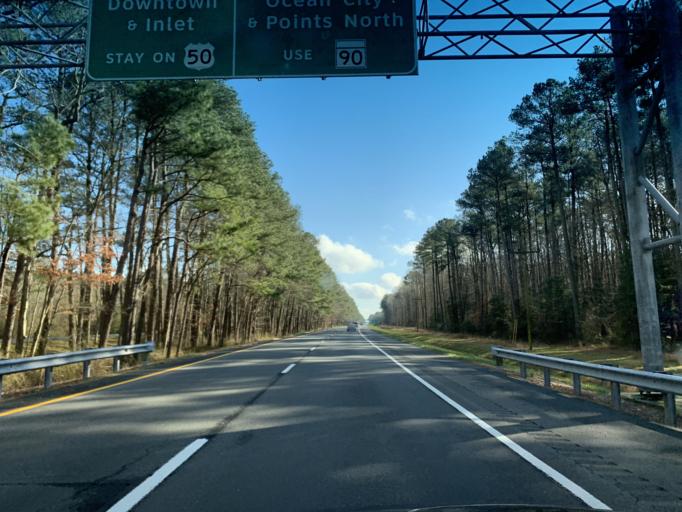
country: US
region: Maryland
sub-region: Worcester County
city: Berlin
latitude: 38.3778
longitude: -75.2878
